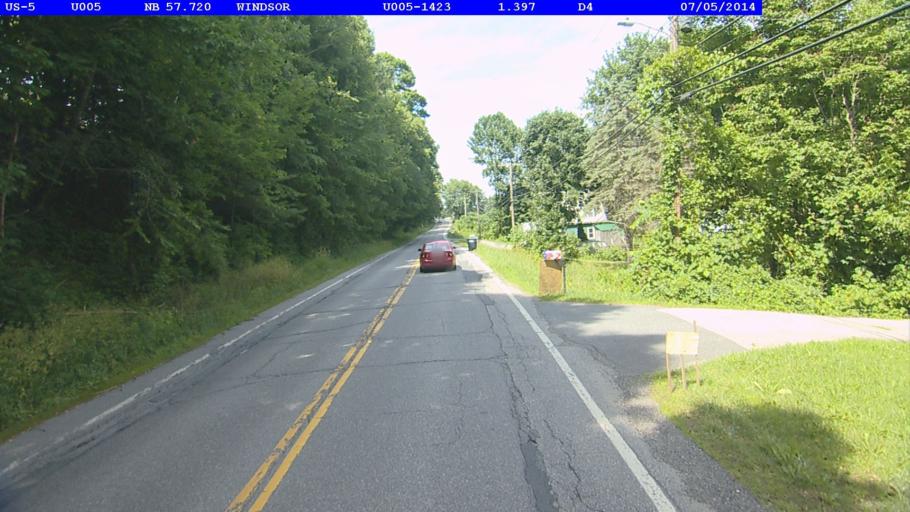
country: US
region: Vermont
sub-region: Windsor County
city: Windsor
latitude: 43.4485
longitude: -72.3963
